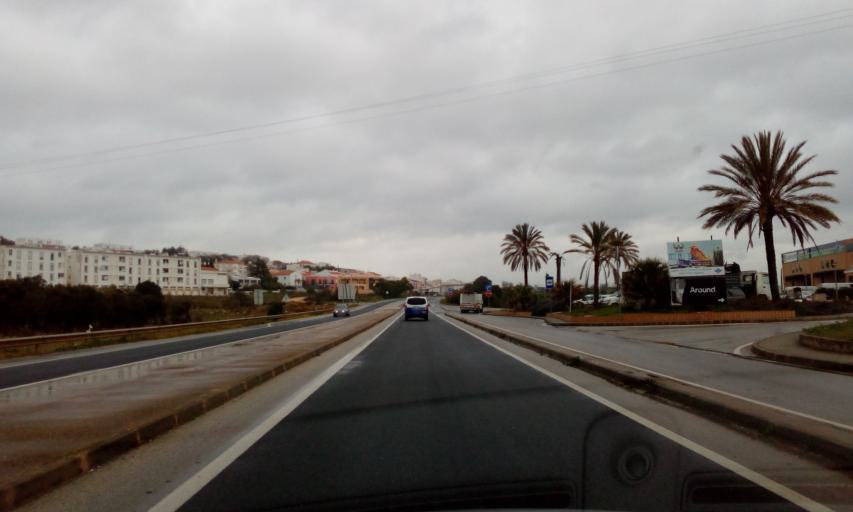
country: PT
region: Faro
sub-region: Lagos
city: Lagos
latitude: 37.1266
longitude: -8.6715
